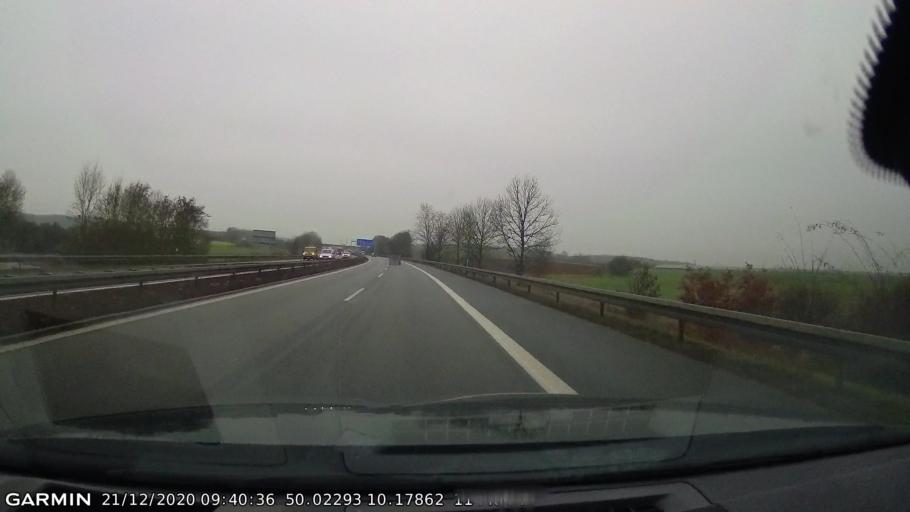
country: DE
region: Bavaria
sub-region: Regierungsbezirk Unterfranken
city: Bergrheinfeld
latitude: 50.0230
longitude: 10.1783
